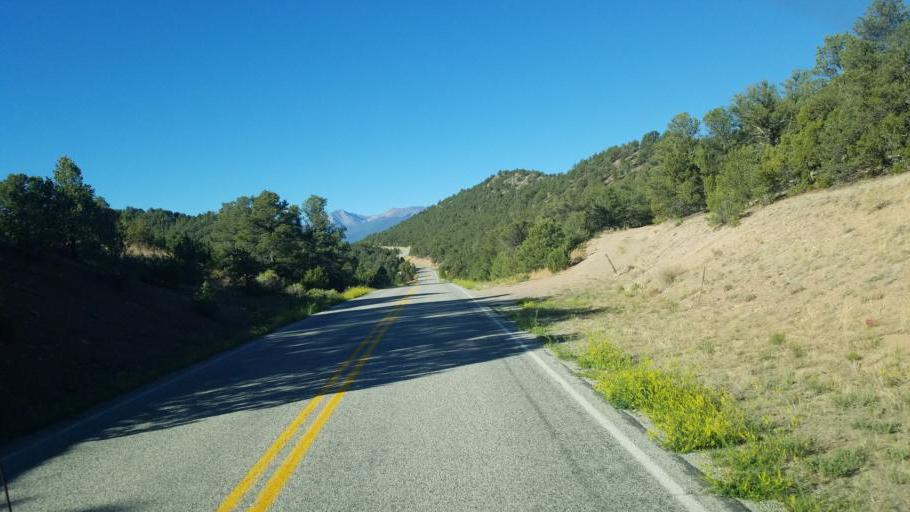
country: US
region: Colorado
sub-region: Custer County
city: Westcliffe
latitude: 38.3826
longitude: -105.5812
